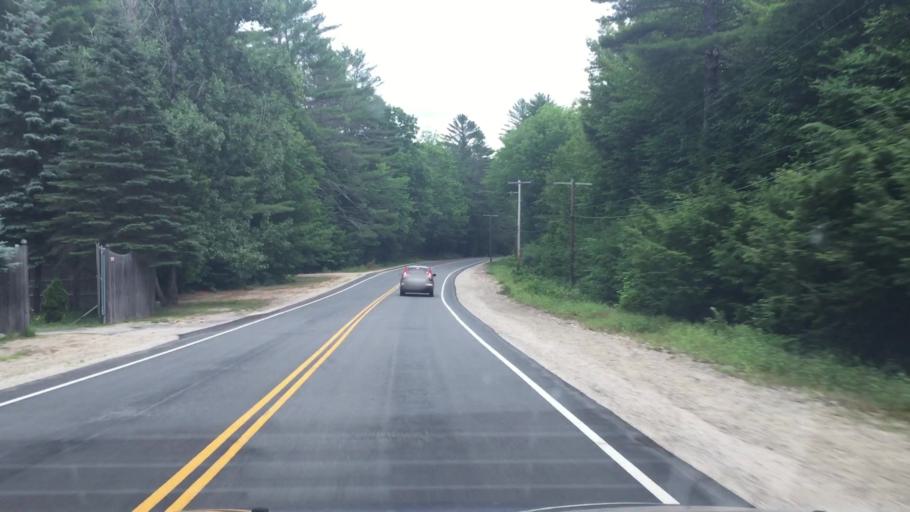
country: US
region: New Hampshire
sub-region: Carroll County
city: Tamworth
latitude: 43.8798
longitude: -71.2328
